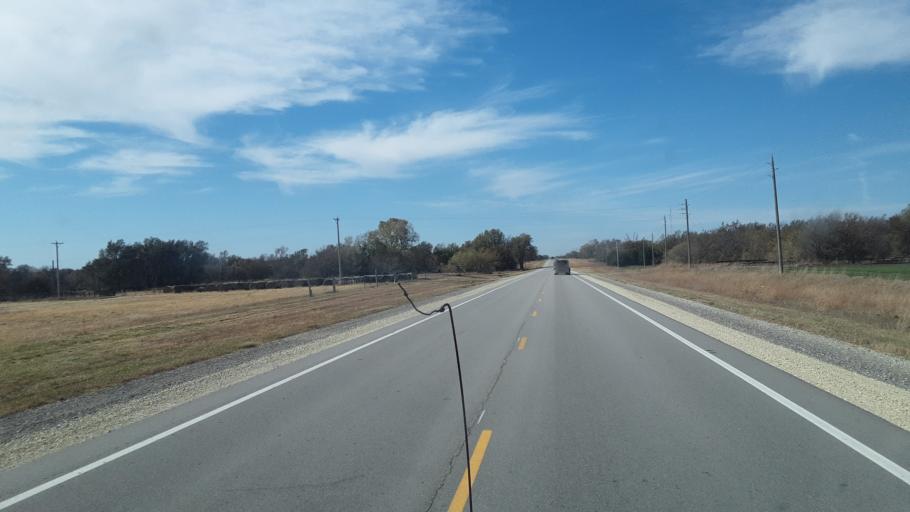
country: US
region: Kansas
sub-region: McPherson County
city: McPherson
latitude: 38.3769
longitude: -97.4919
